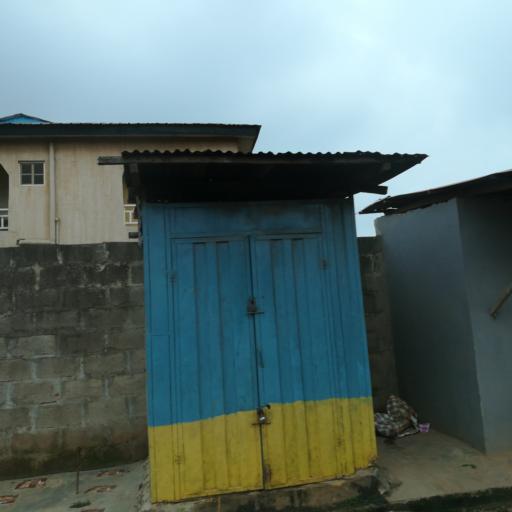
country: NG
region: Lagos
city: Agege
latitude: 6.5923
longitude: 3.2992
